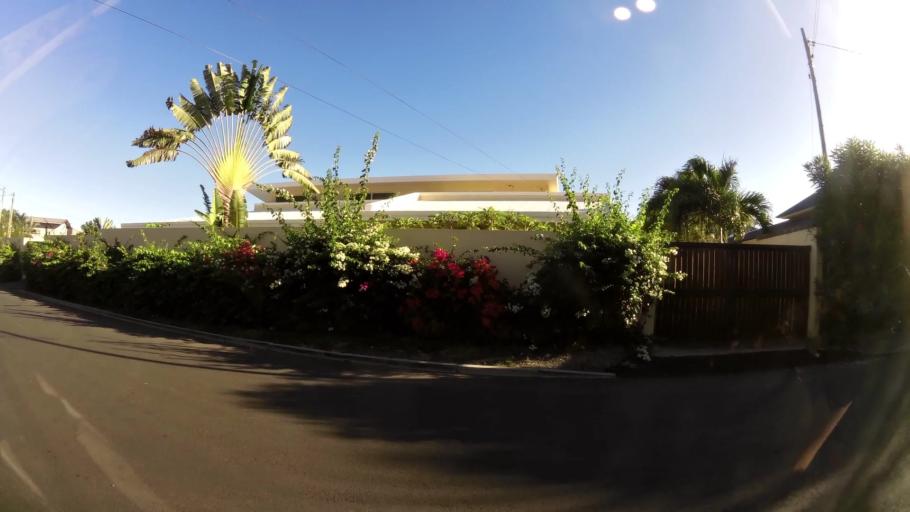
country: MU
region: Black River
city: Tamarin
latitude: -20.3355
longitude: 57.3778
